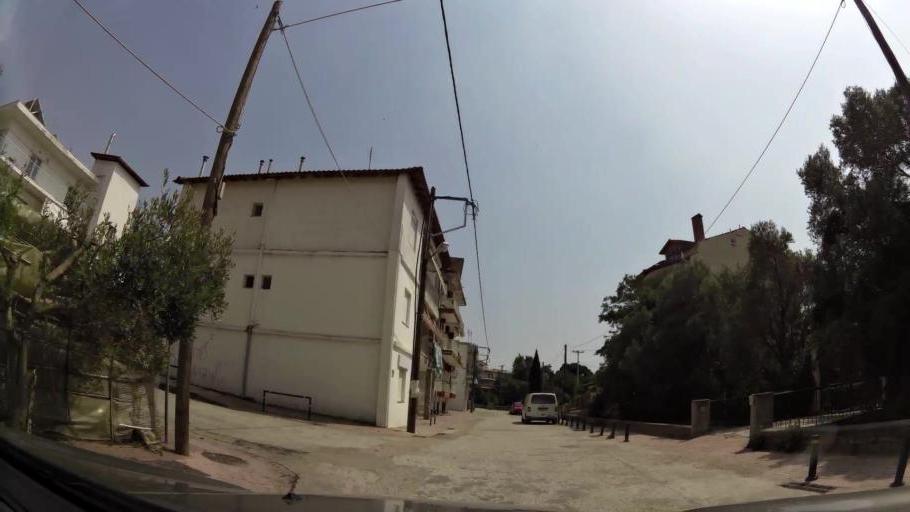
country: GR
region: Central Macedonia
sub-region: Nomos Thessalonikis
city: Diavata
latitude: 40.6894
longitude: 22.8539
